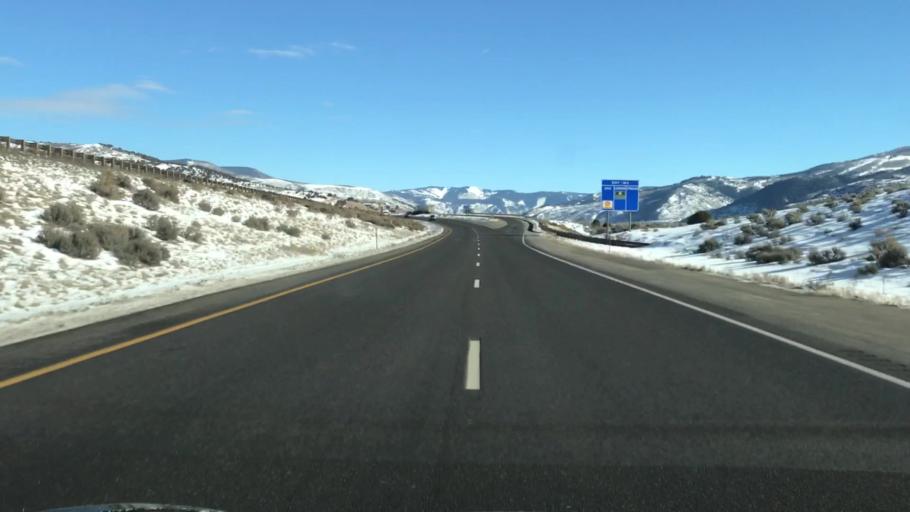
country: US
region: Colorado
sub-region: Eagle County
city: Edwards
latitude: 39.6538
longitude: -106.6136
